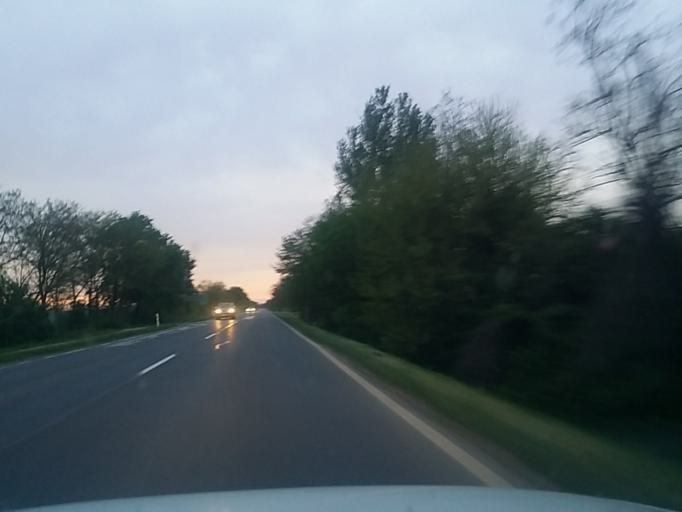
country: HU
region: Bekes
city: Csorvas
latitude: 46.7178
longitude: 20.9342
